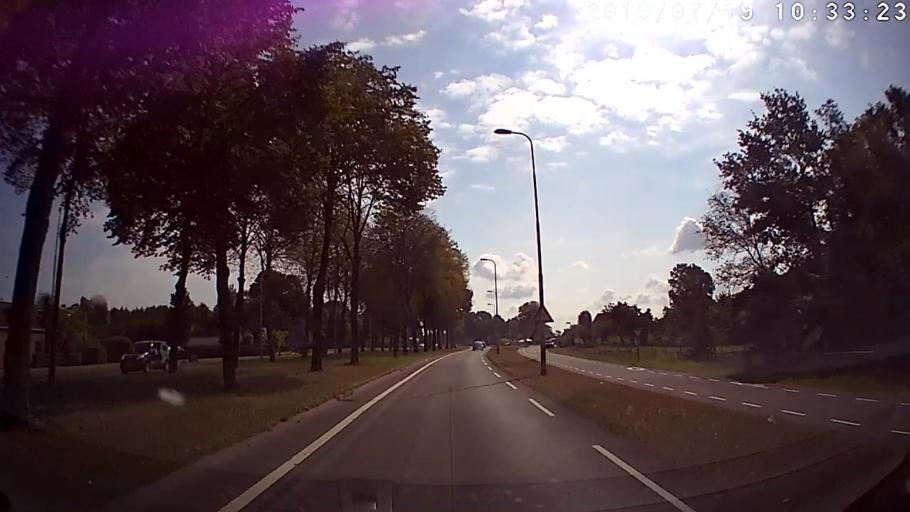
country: NL
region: Drenthe
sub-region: Gemeente Hoogeveen
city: Hoogeveen
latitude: 52.6032
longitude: 6.4131
